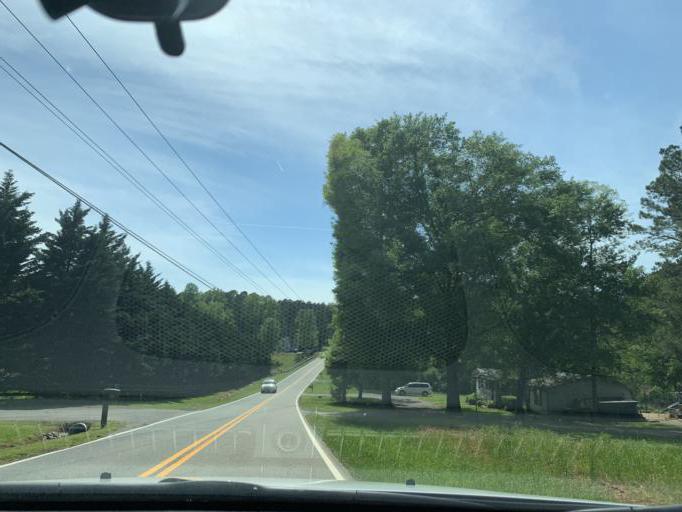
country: US
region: Georgia
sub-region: Forsyth County
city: Cumming
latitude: 34.2650
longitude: -84.1840
